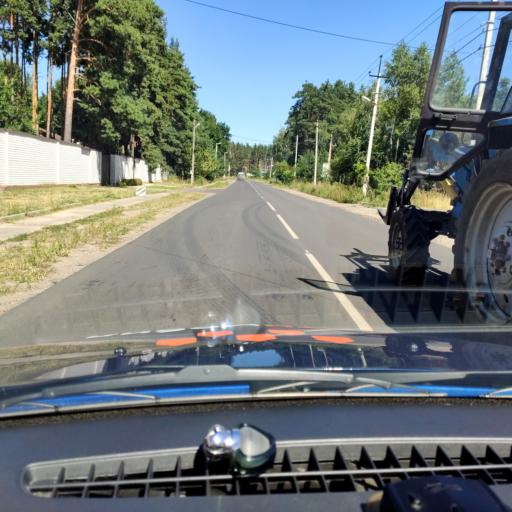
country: RU
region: Voronezj
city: Podgornoye
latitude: 51.7847
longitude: 39.1434
